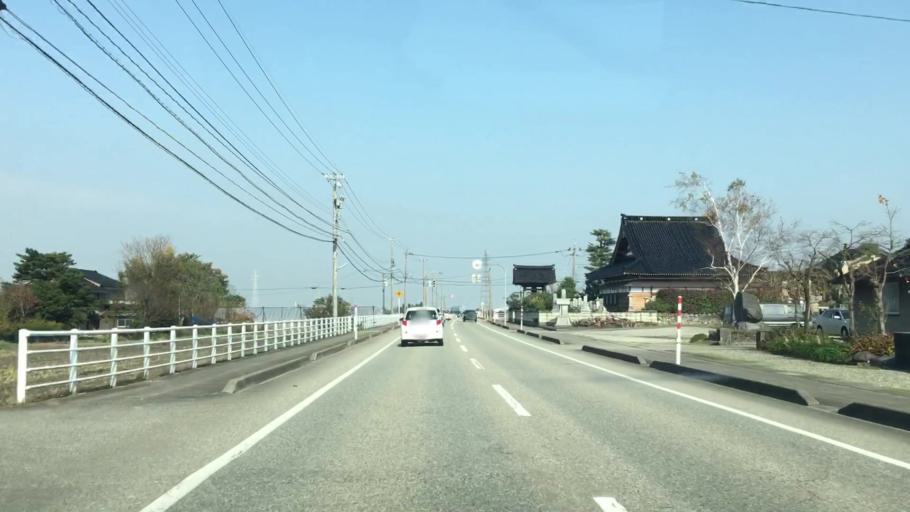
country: JP
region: Toyama
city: Yatsuomachi-higashikumisaka
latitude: 36.6018
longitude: 137.1915
